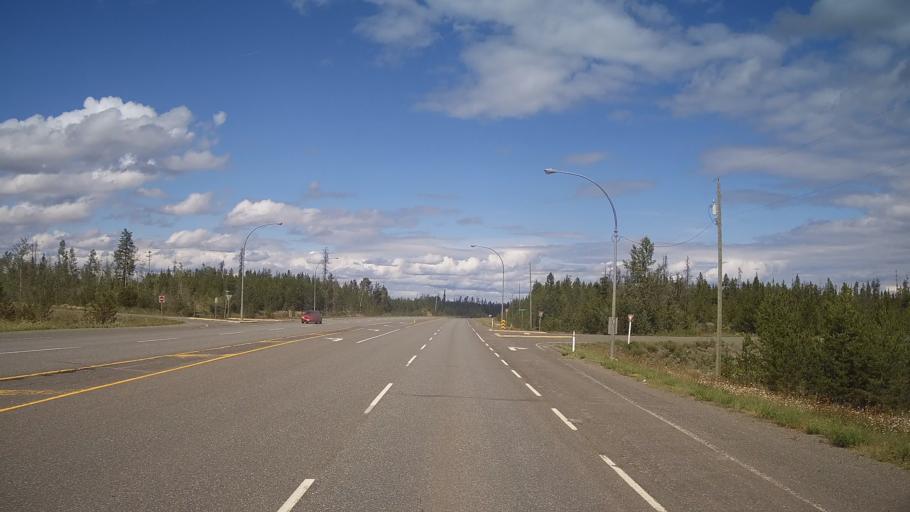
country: CA
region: British Columbia
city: Cache Creek
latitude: 51.5460
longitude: -121.3634
